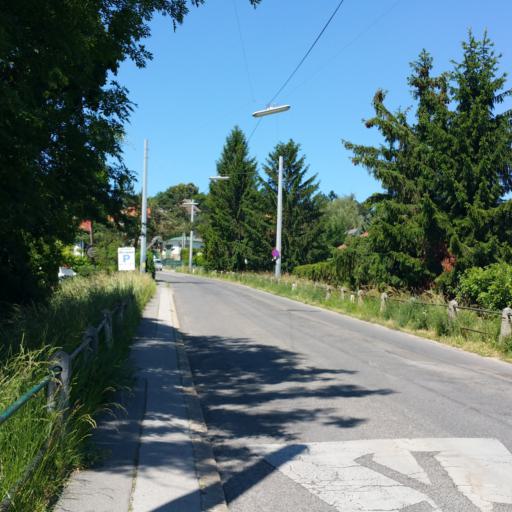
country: AT
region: Vienna
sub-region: Wien Stadt
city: Vienna
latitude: 48.2136
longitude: 16.2878
